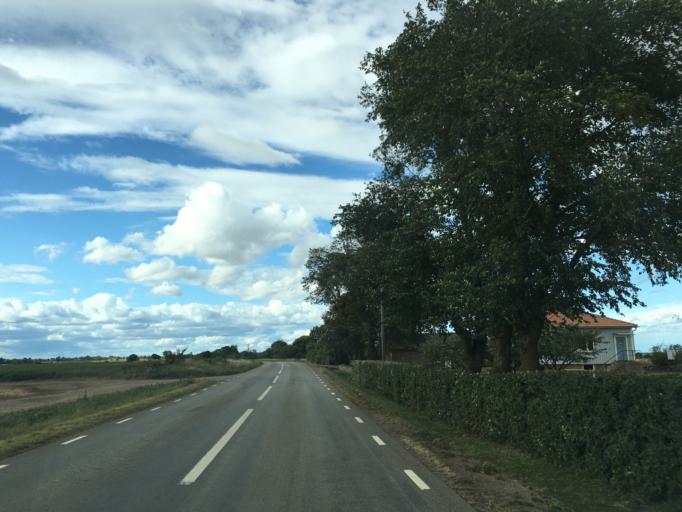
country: SE
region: Kalmar
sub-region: Morbylanga Kommun
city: Moerbylanga
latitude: 56.4217
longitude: 16.4357
